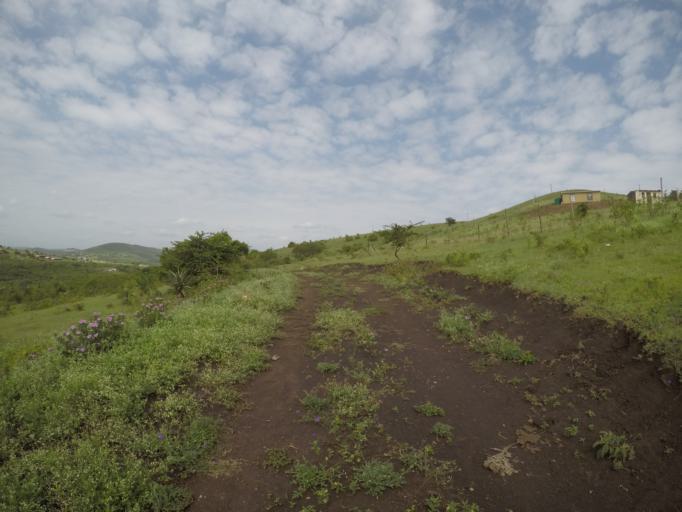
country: ZA
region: KwaZulu-Natal
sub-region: uThungulu District Municipality
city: Empangeni
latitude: -28.6171
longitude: 31.8999
